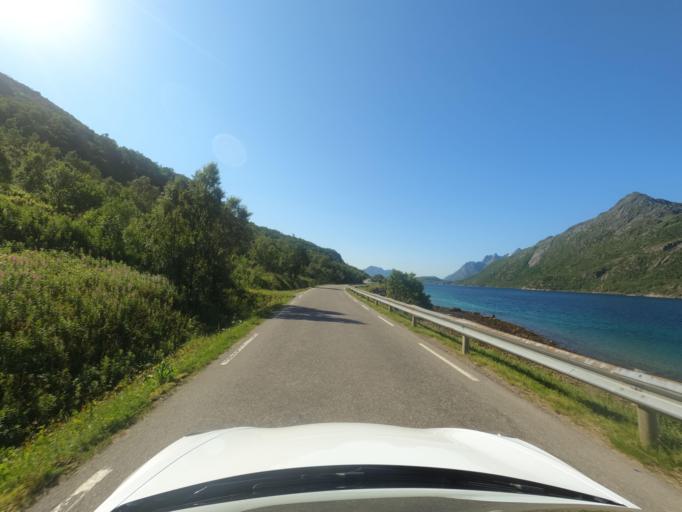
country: NO
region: Nordland
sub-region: Hadsel
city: Stokmarknes
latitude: 68.3902
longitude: 15.1005
